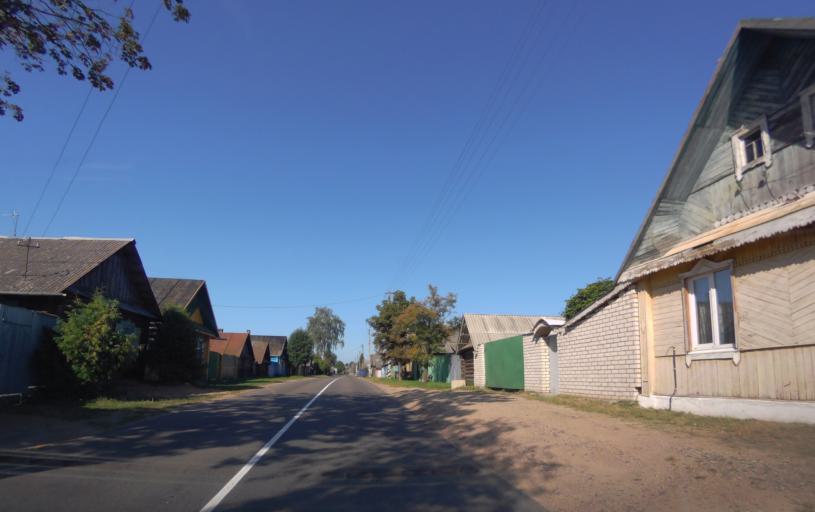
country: BY
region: Minsk
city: Horad Barysaw
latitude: 54.2569
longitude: 28.3987
